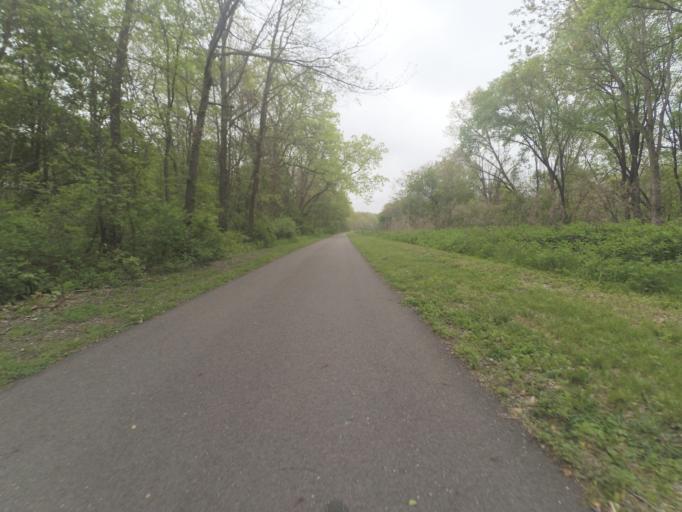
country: US
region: Ohio
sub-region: Portage County
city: Kent
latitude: 41.1716
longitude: -81.3171
